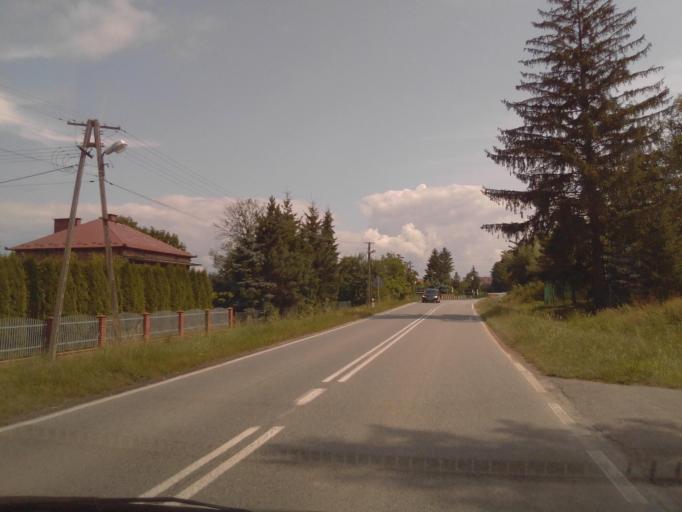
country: PL
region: Subcarpathian Voivodeship
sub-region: Powiat ropczycko-sedziszowski
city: Ropczyce
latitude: 50.0373
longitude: 21.5805
